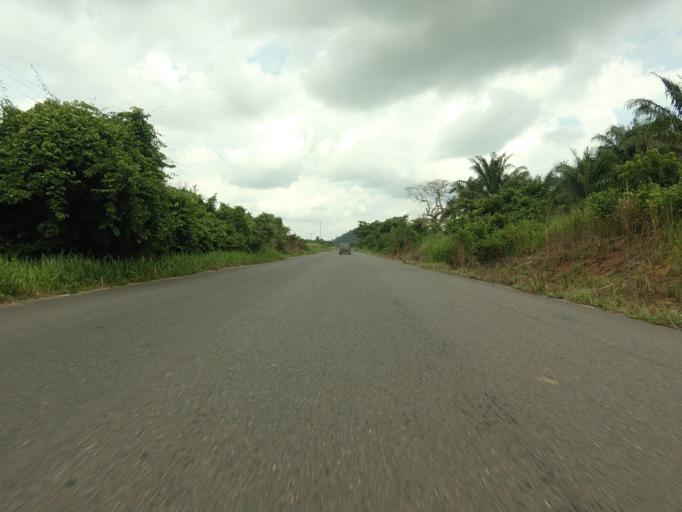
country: GH
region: Volta
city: Ho
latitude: 6.4377
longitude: 0.1717
